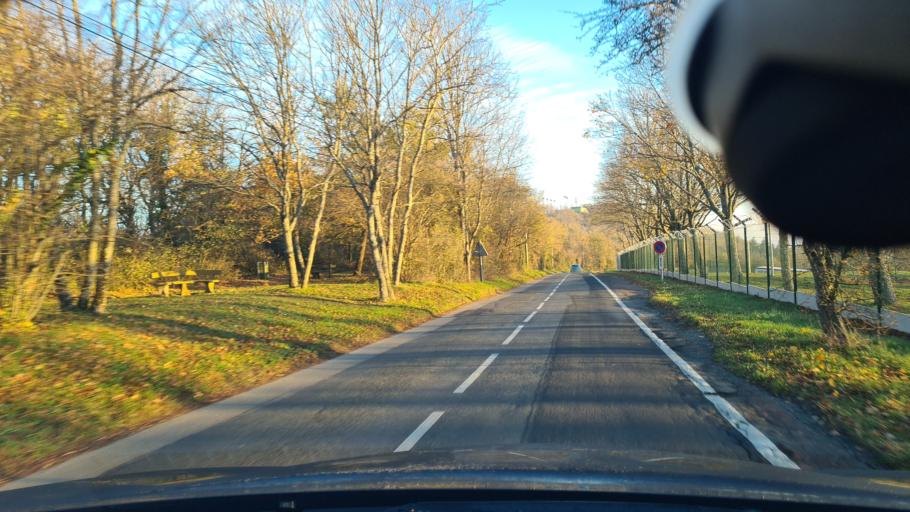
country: FR
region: Rhone-Alpes
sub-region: Departement du Rhone
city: Limonest
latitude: 45.8553
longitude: 4.7859
